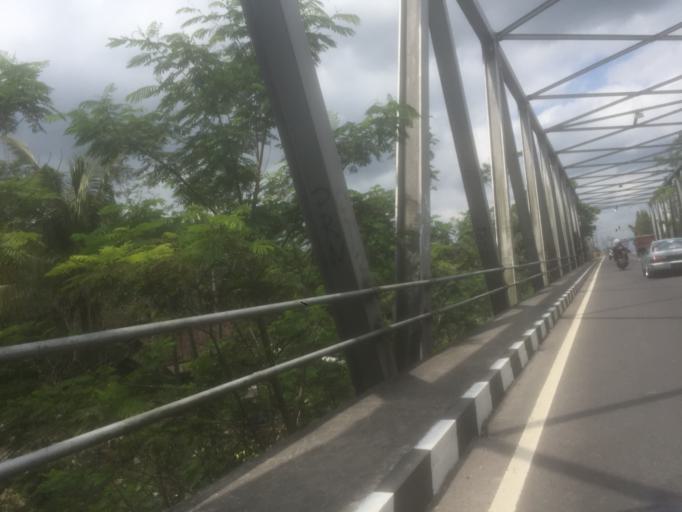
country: ID
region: Central Java
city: Muntilan
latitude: -7.6445
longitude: 110.3238
